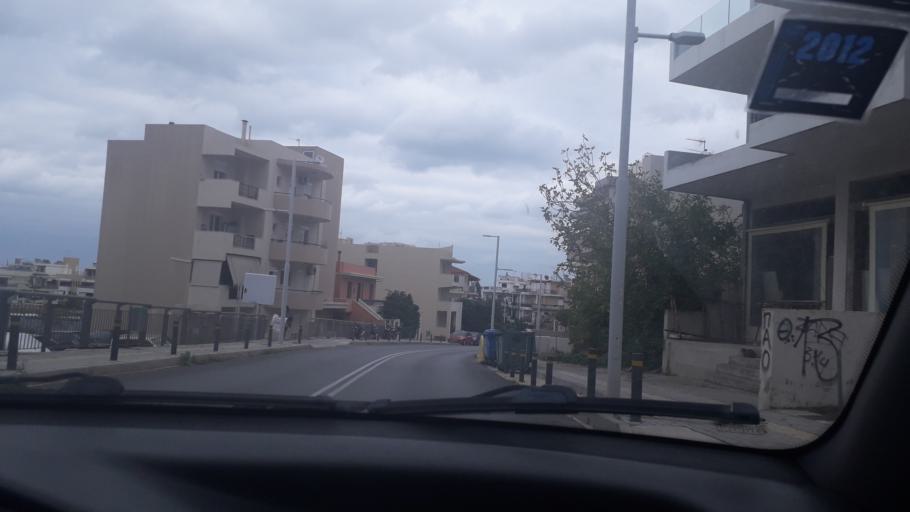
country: GR
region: Crete
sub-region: Nomos Rethymnis
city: Rethymno
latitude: 35.3578
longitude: 24.4753
